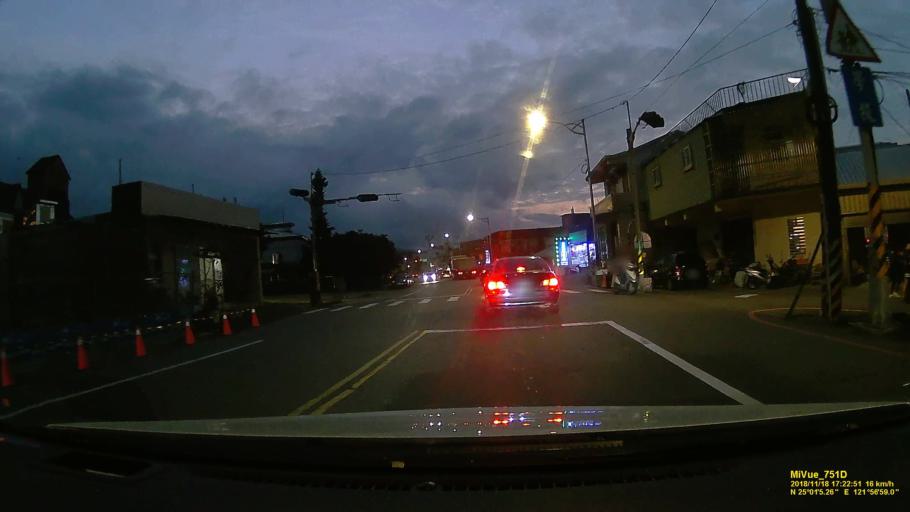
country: TW
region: Taiwan
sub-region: Keelung
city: Keelung
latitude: 25.0181
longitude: 121.9497
